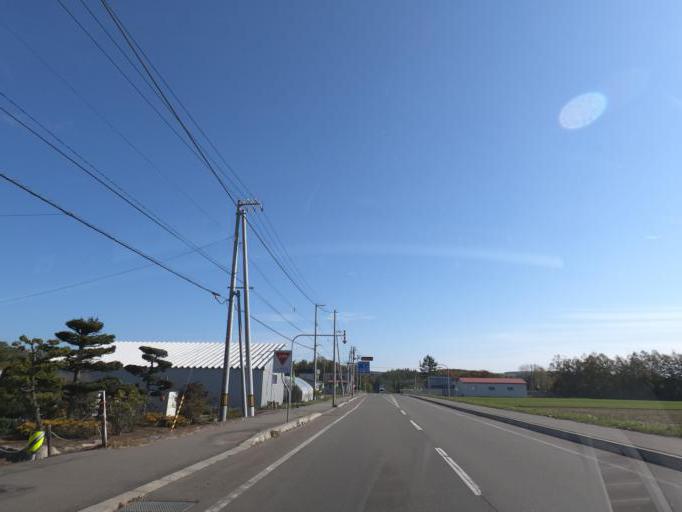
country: JP
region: Hokkaido
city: Otofuke
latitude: 42.9603
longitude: 143.2482
